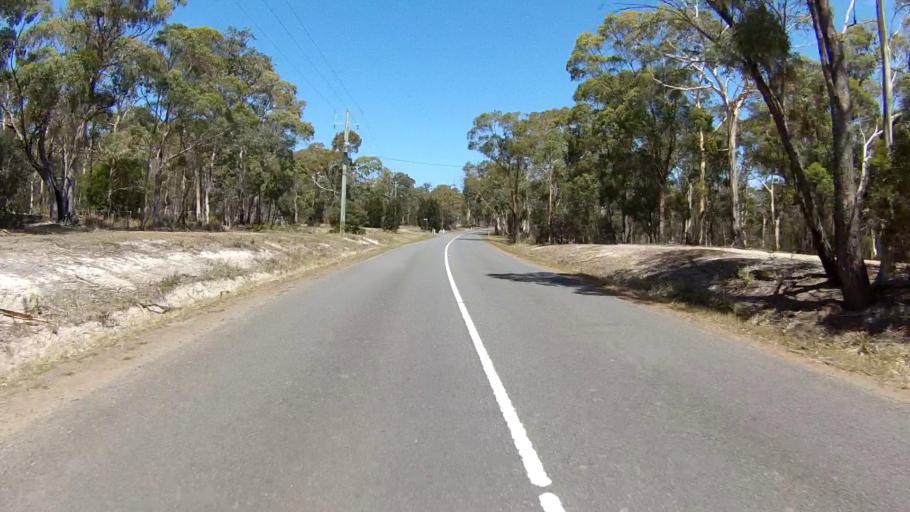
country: AU
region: Tasmania
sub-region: Clarence
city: Sandford
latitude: -42.9698
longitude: 147.4797
